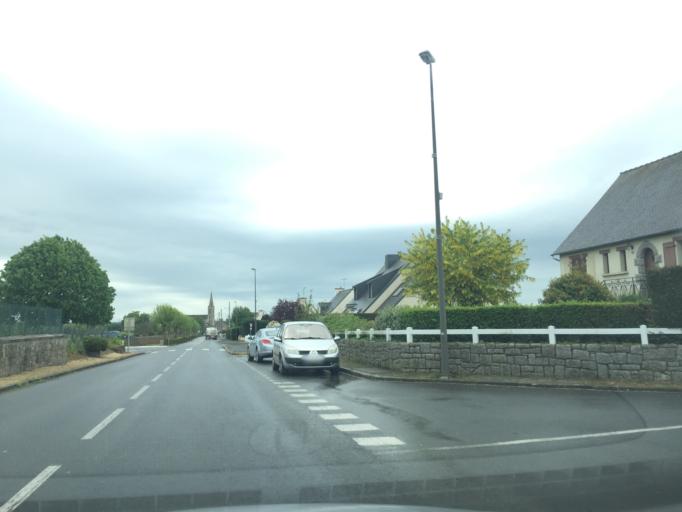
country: FR
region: Brittany
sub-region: Departement des Cotes-d'Armor
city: Crehen
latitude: 48.5499
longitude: -2.2325
